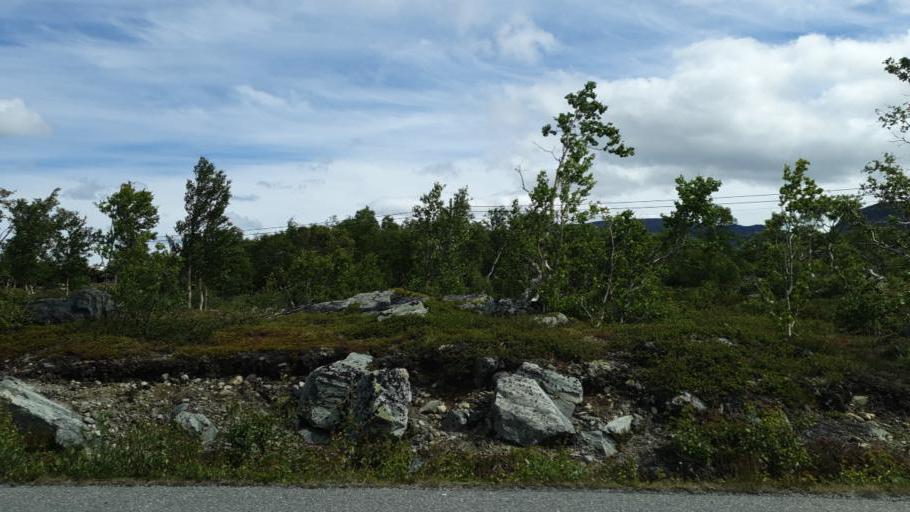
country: NO
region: Oppland
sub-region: Oystre Slidre
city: Heggenes
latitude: 61.4871
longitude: 8.8302
